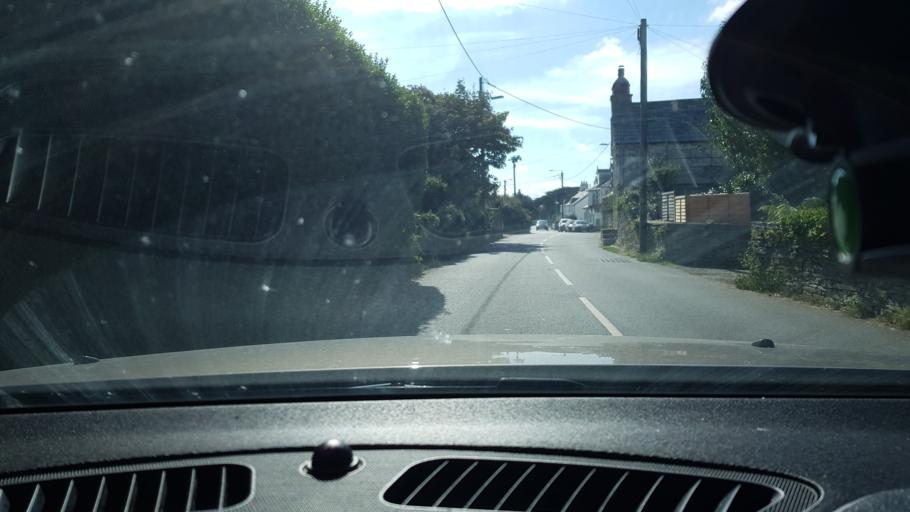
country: GB
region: England
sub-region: Cornwall
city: Tintagel
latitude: 50.6673
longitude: -4.7374
